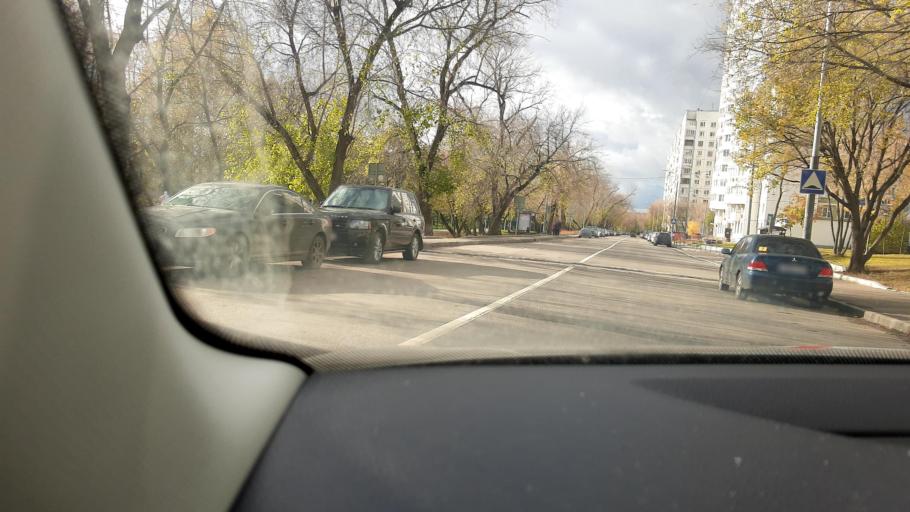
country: RU
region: Moscow
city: Kolomenskoye
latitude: 55.6755
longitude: 37.6948
